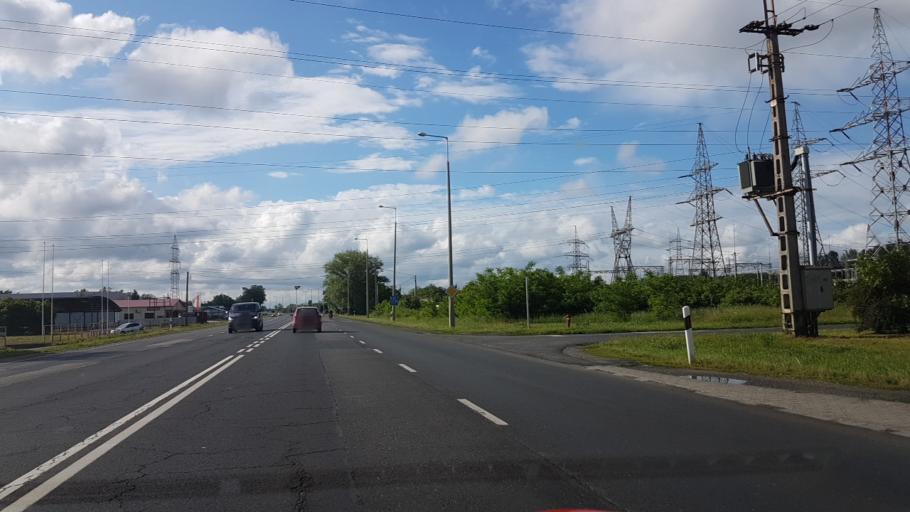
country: HU
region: Hajdu-Bihar
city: Debrecen
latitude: 47.5650
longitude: 21.5999
